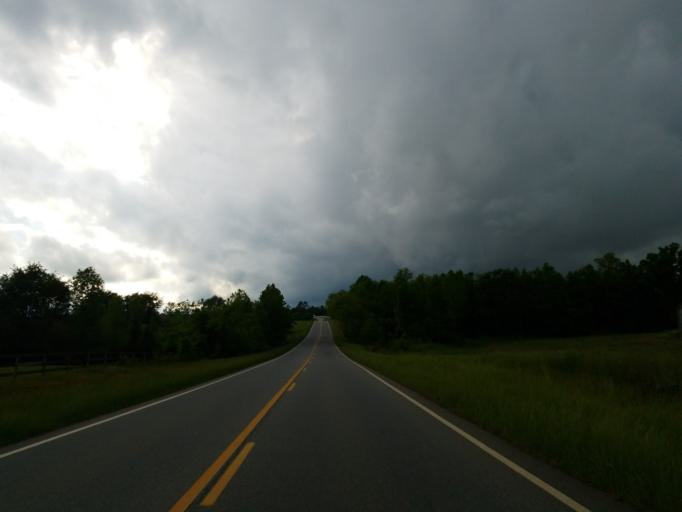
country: US
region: Georgia
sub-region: Dooly County
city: Unadilla
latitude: 32.3398
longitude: -83.7788
